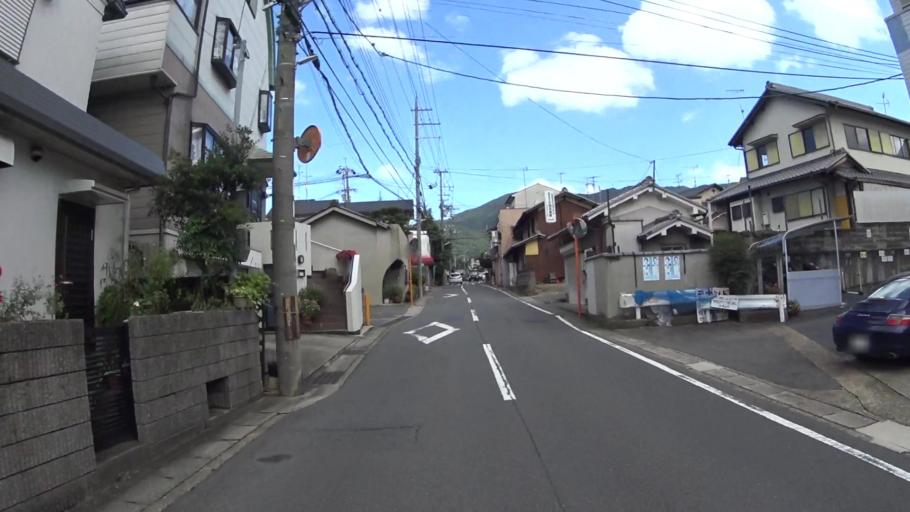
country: JP
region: Kyoto
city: Uji
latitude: 34.9448
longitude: 135.8150
